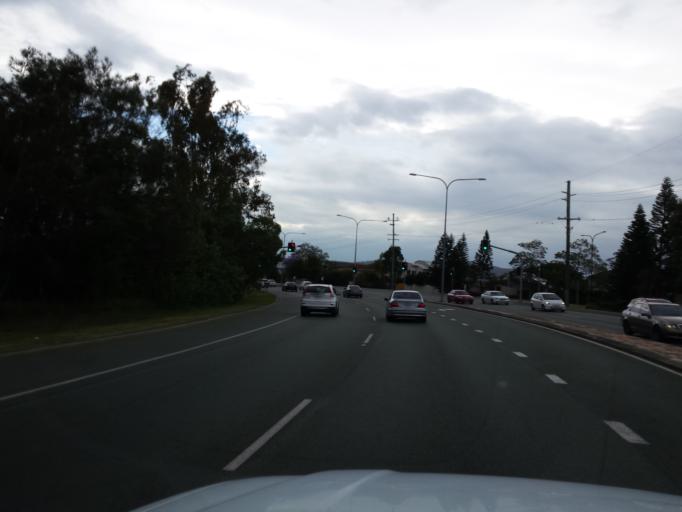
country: AU
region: Queensland
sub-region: Gold Coast
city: Oxenford
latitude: -27.8826
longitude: 153.3248
